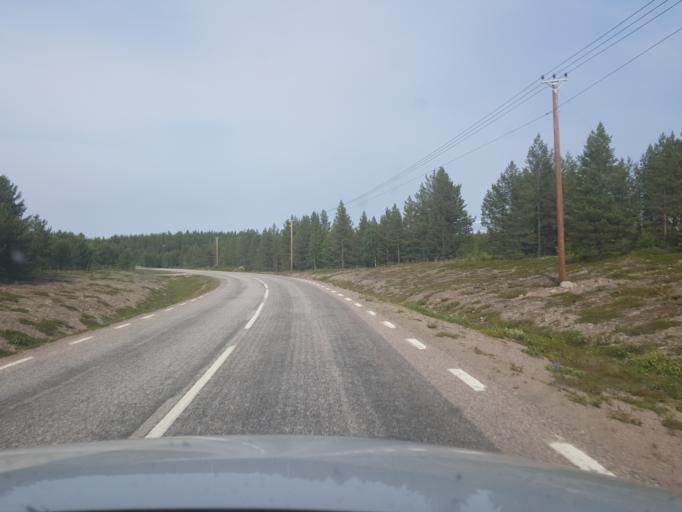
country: SE
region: Norrbotten
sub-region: Arjeplogs Kommun
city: Arjeplog
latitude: 65.8442
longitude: 18.0378
